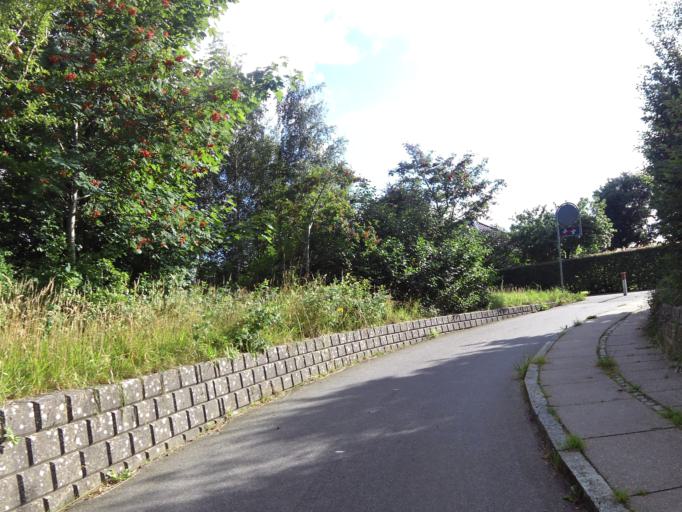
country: DK
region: South Denmark
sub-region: Haderslev Kommune
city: Vojens
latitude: 55.1958
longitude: 9.3031
